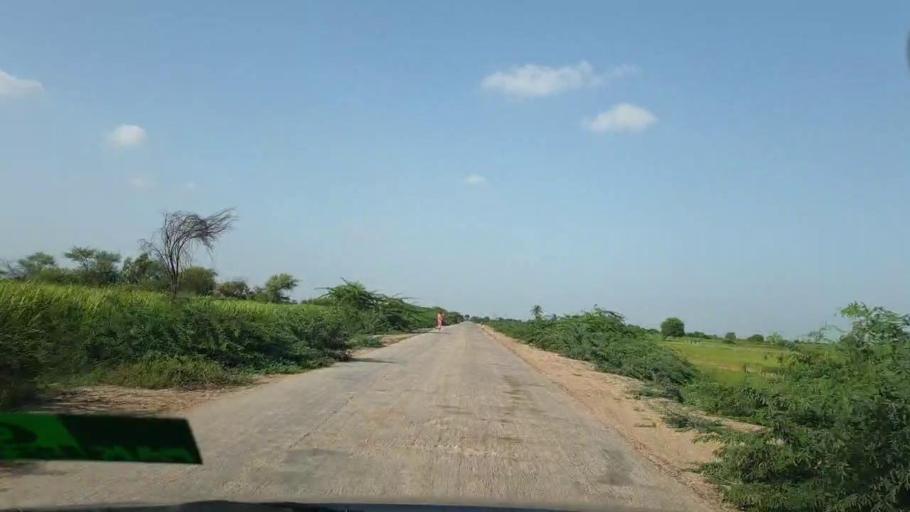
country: PK
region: Sindh
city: Tando Bago
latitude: 24.7121
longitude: 69.1928
